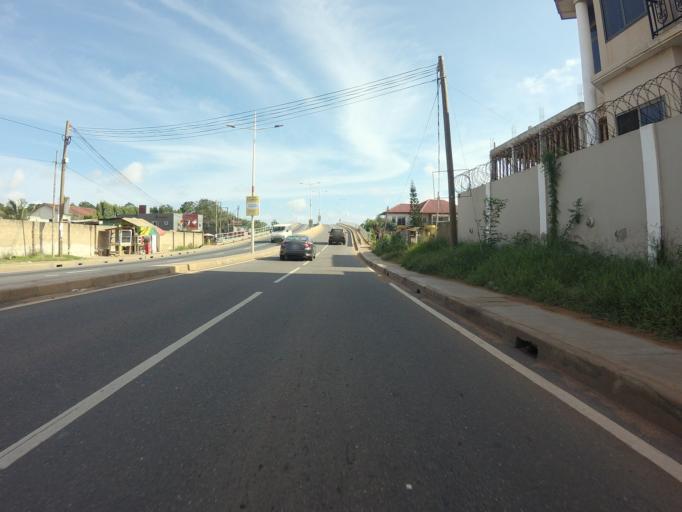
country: GH
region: Greater Accra
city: Medina Estates
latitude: 5.6211
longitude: -0.1528
